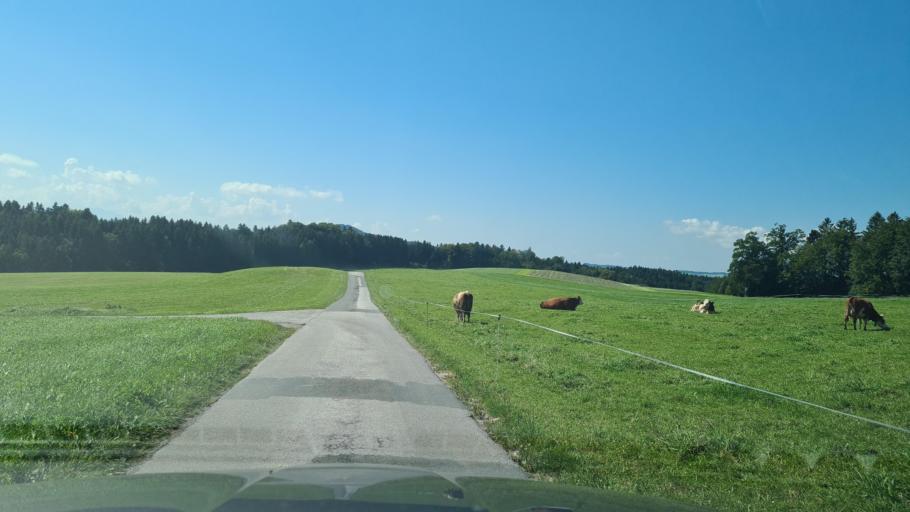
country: AT
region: Salzburg
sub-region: Politischer Bezirk Salzburg-Umgebung
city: Schleedorf
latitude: 47.9674
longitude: 13.1528
